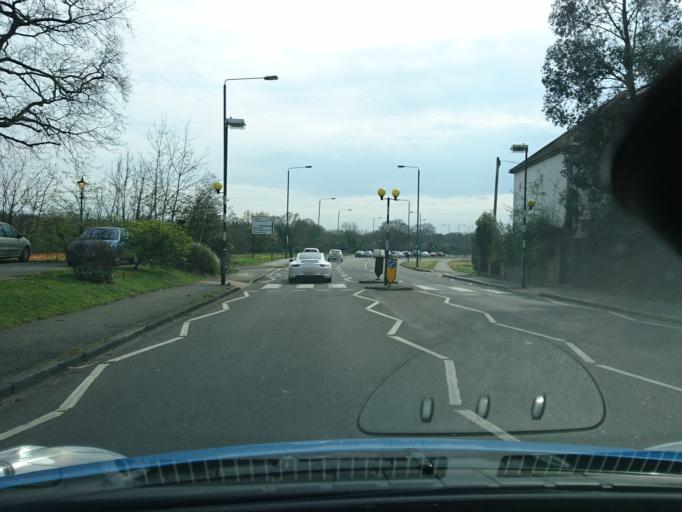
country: GB
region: England
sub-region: Greater London
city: Walthamstow
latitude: 51.5856
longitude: 0.0065
